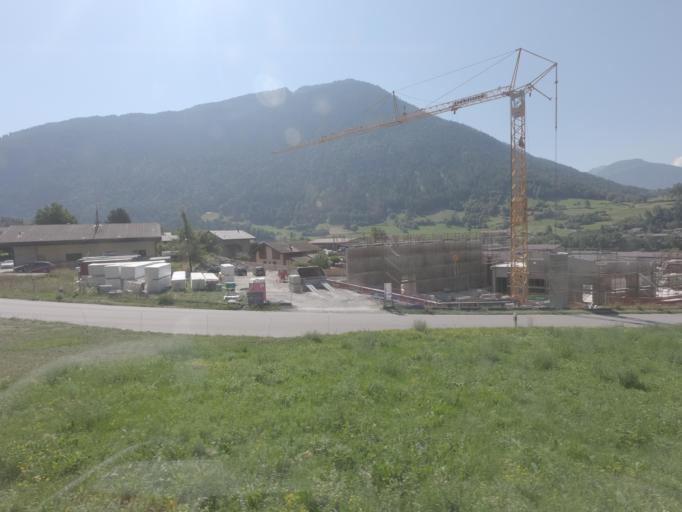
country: CH
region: Valais
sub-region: Martigny District
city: Charrat-les-Chenes
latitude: 46.0826
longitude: 7.1585
